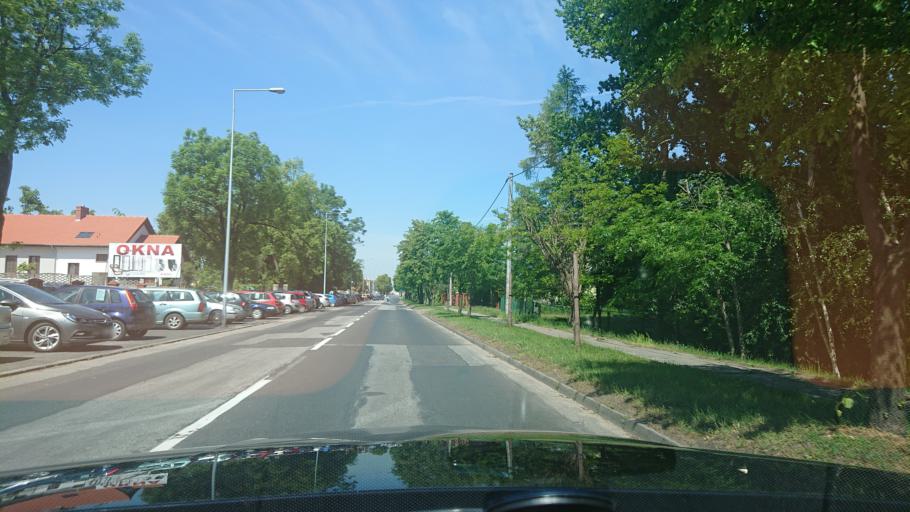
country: PL
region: Greater Poland Voivodeship
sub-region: Powiat gnieznienski
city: Gniezno
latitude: 52.5185
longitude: 17.6081
